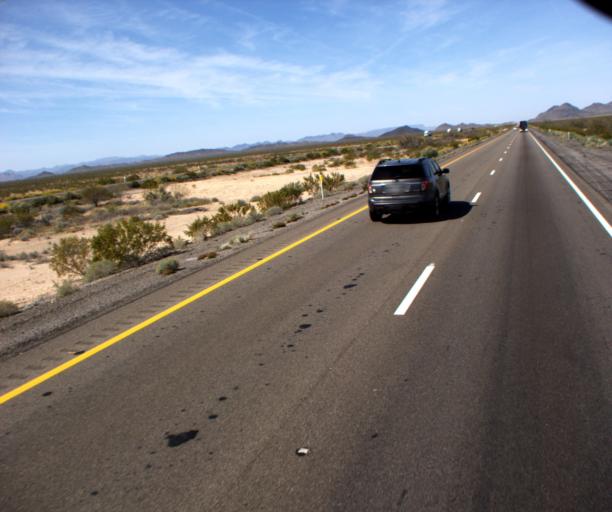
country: US
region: Arizona
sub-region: La Paz County
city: Salome
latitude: 33.5979
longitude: -113.5431
